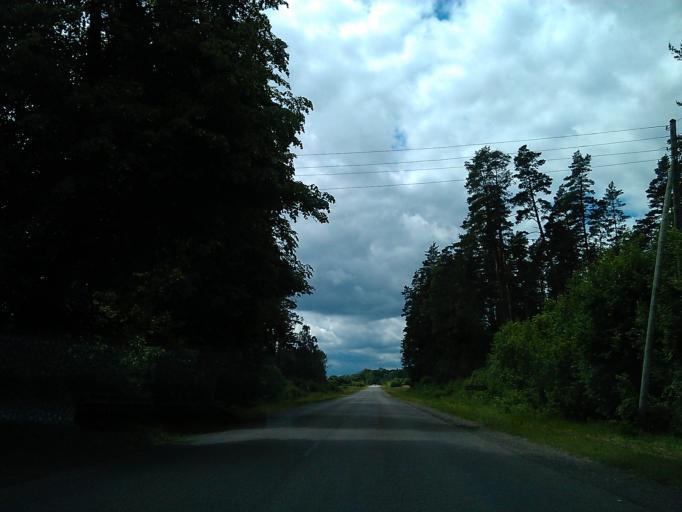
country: LV
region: Talsu Rajons
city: Stende
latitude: 57.0829
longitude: 22.2998
